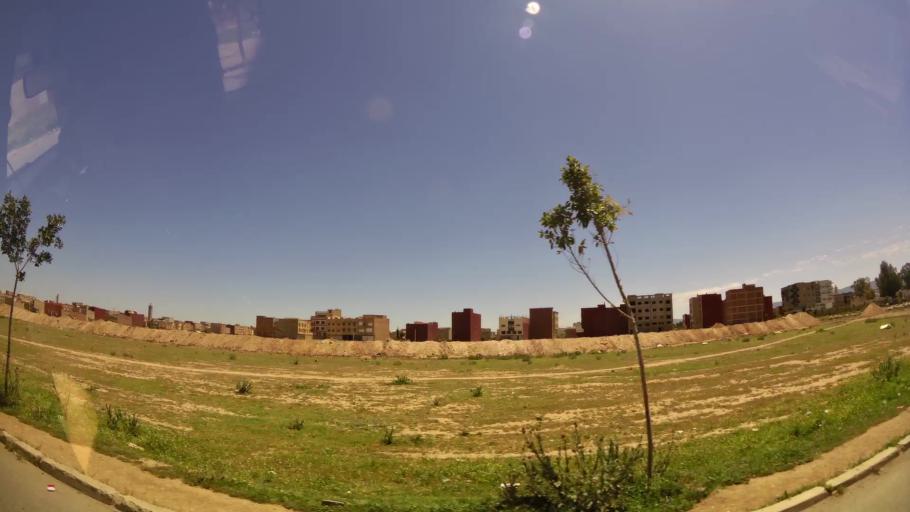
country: MA
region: Oriental
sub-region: Oujda-Angad
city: Oujda
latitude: 34.6714
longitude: -1.8821
